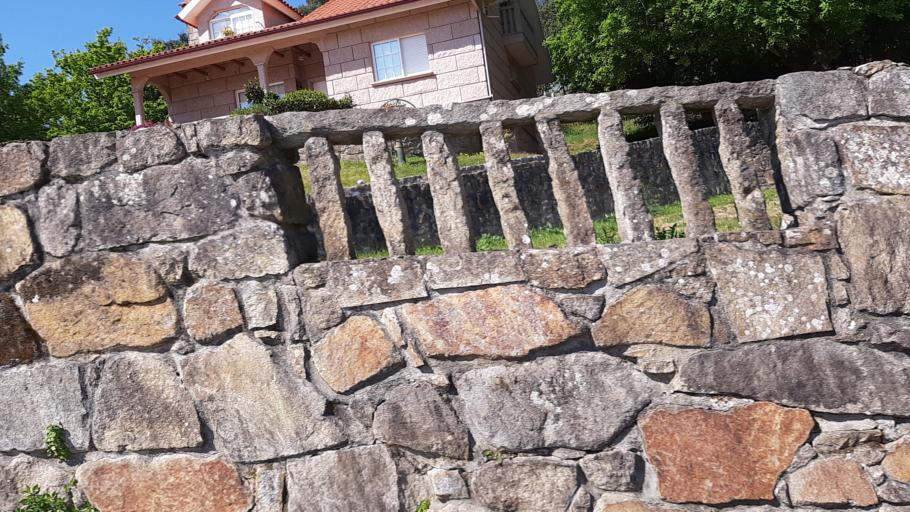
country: ES
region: Galicia
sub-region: Provincia de Pontevedra
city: O Rosal
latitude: 41.9375
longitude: -8.8562
